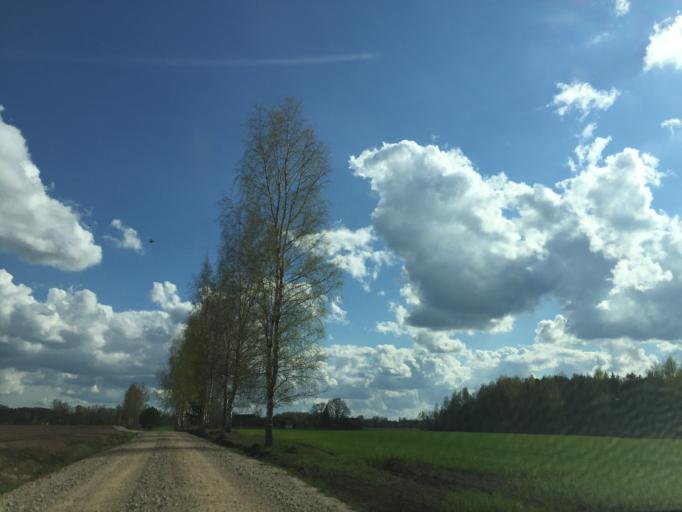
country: LV
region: Beverina
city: Murmuiza
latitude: 57.4248
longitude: 25.5496
